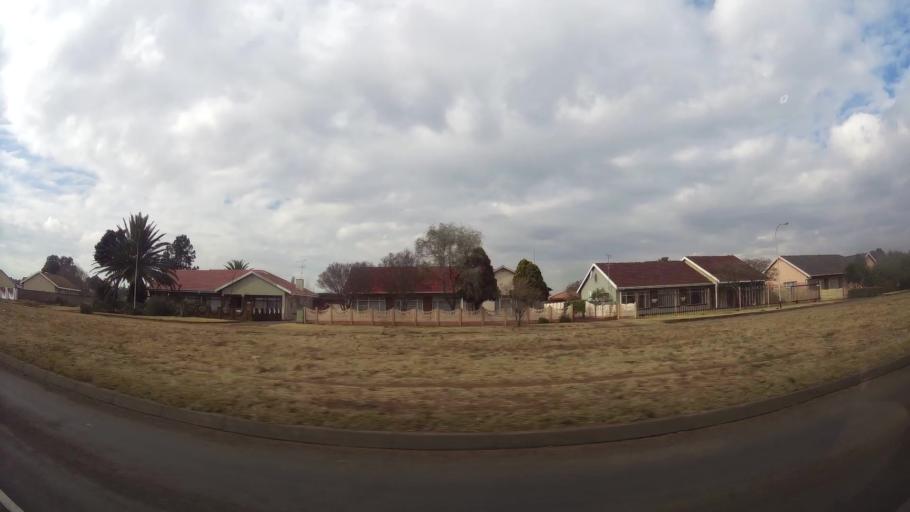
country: ZA
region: Gauteng
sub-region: Sedibeng District Municipality
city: Meyerton
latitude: -26.5900
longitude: 28.0011
